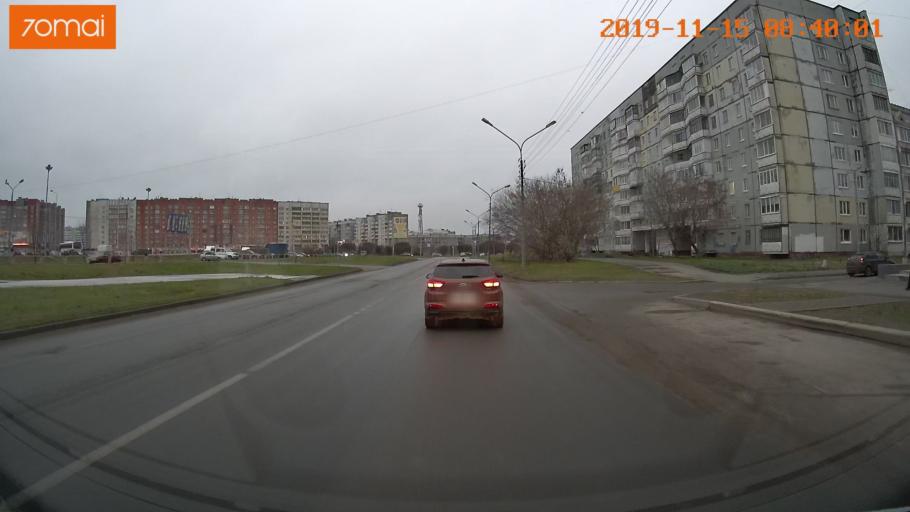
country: RU
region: Vologda
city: Cherepovets
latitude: 59.0937
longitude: 37.9187
